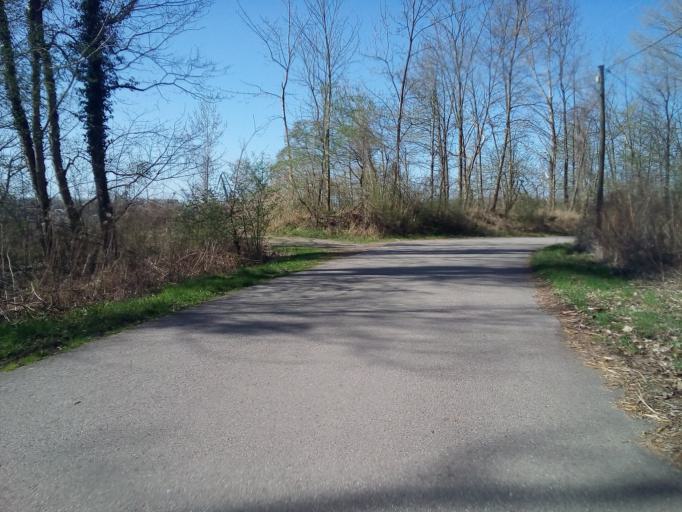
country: DE
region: Baden-Wuerttemberg
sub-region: Freiburg Region
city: Rheinau
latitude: 48.6860
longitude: 7.9328
